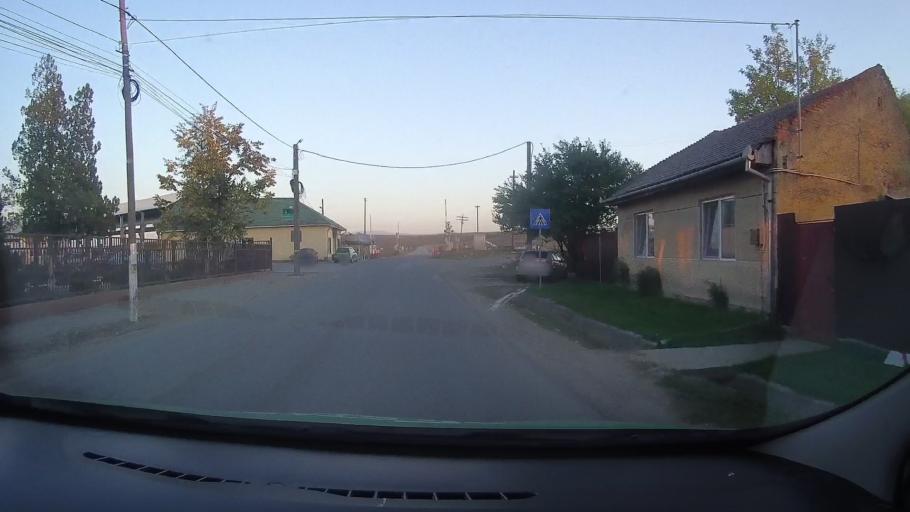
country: RO
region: Timis
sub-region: Comuna Manastiur
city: Manastiur
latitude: 45.8284
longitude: 22.0685
